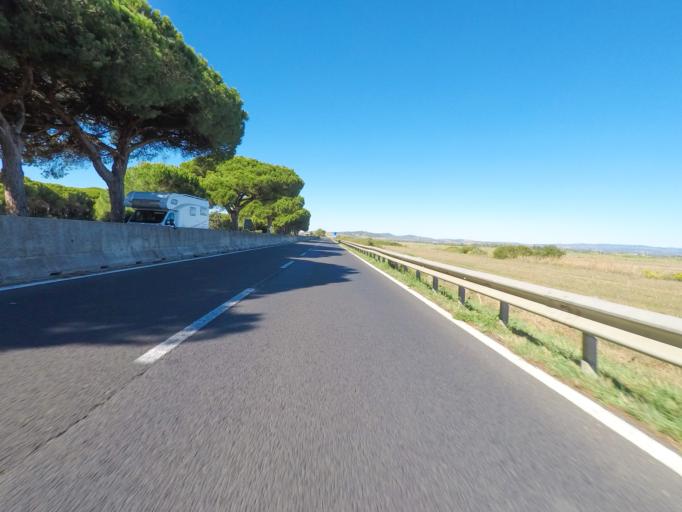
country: IT
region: Tuscany
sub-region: Provincia di Grosseto
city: Albinia
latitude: 42.5171
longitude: 11.1938
